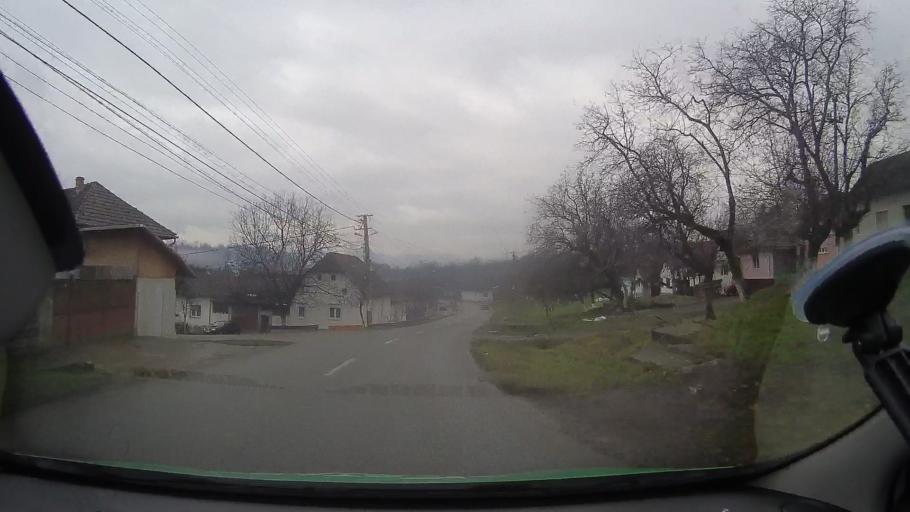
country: RO
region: Arad
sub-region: Comuna Gurahont
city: Gurahont
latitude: 46.2683
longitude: 22.3430
